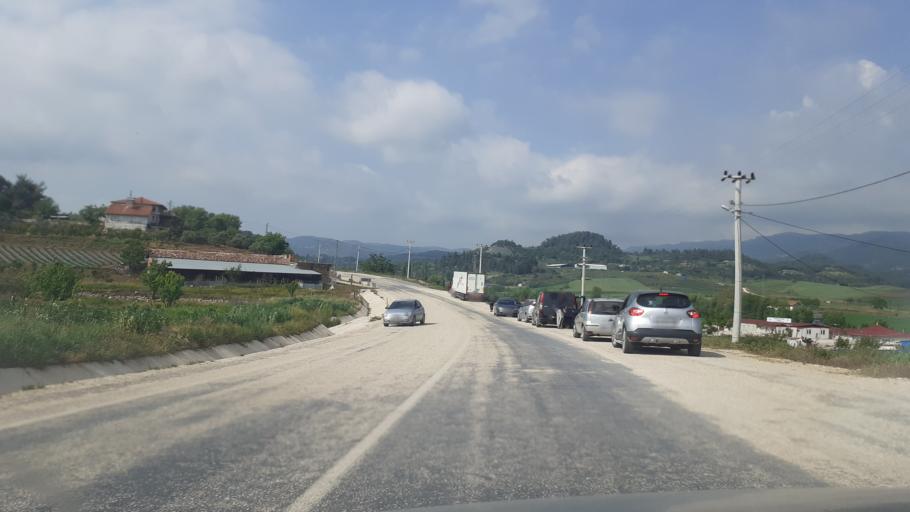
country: TR
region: Hatay
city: Yayladagi
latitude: 35.9094
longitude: 36.0538
